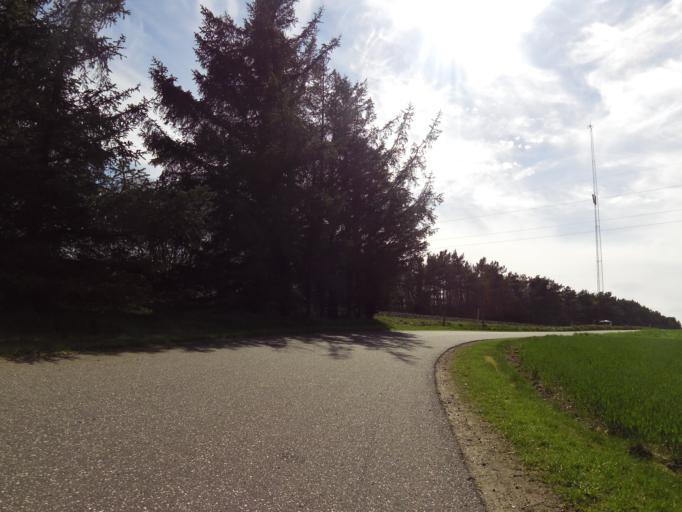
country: DK
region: Central Jutland
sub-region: Skive Kommune
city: Skive
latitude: 56.5637
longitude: 8.9853
